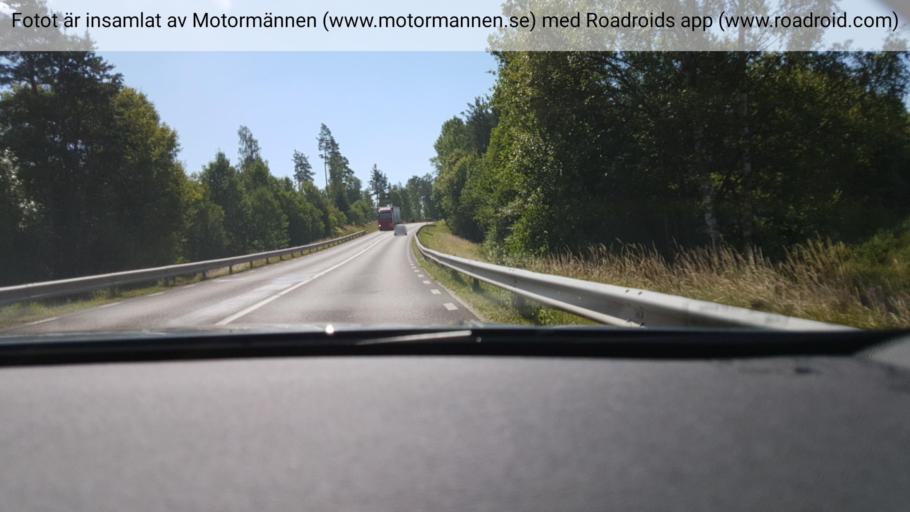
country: SE
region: Joenkoeping
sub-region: Mullsjo Kommun
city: Mullsjoe
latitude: 58.0735
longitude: 13.8017
